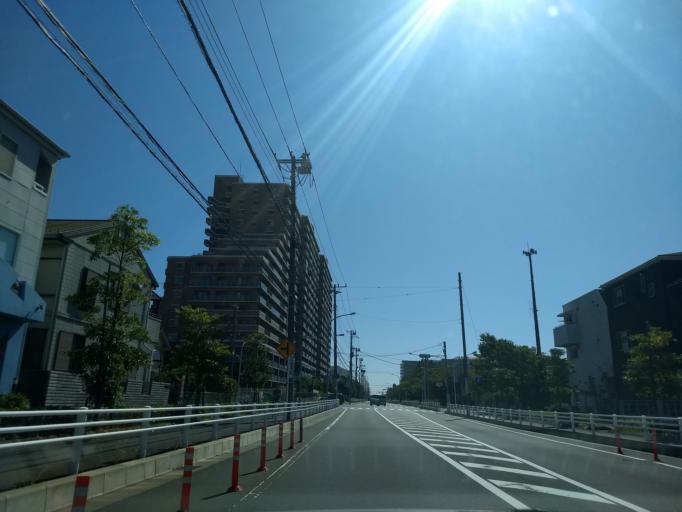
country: JP
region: Tokyo
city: Urayasu
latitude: 35.6382
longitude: 139.9148
